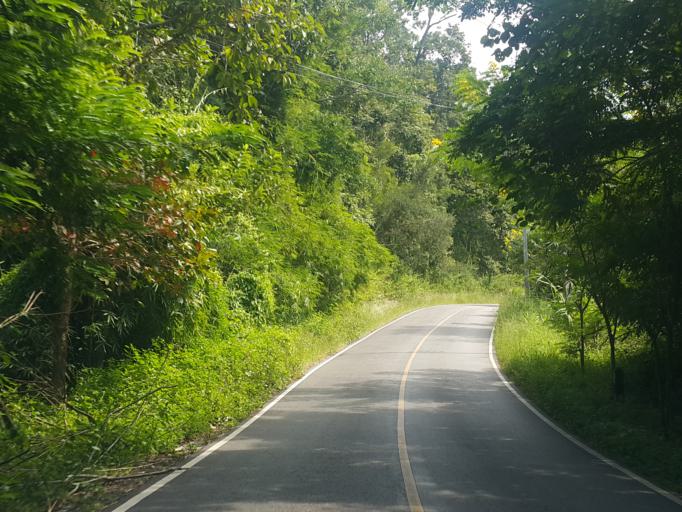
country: TH
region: Chiang Mai
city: Mae On
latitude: 18.8629
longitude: 99.2968
